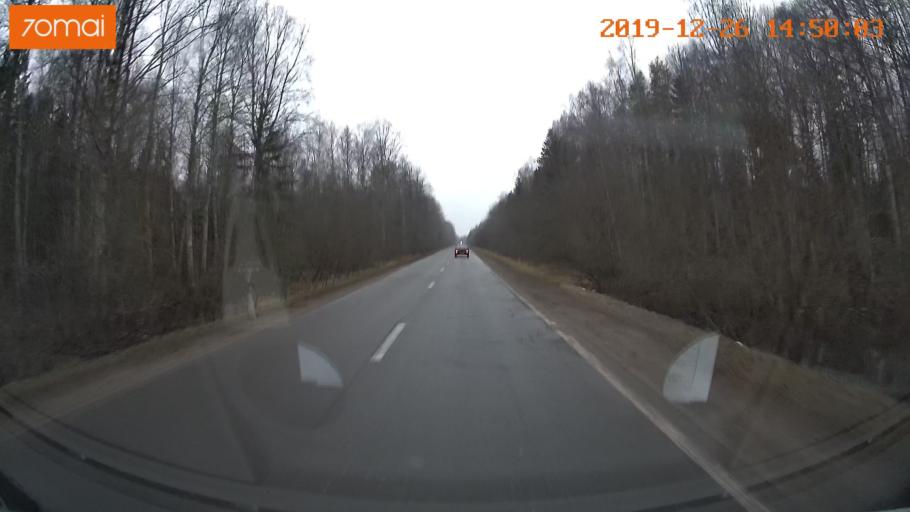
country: RU
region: Jaroslavl
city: Poshekhon'ye
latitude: 58.3352
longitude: 38.9325
